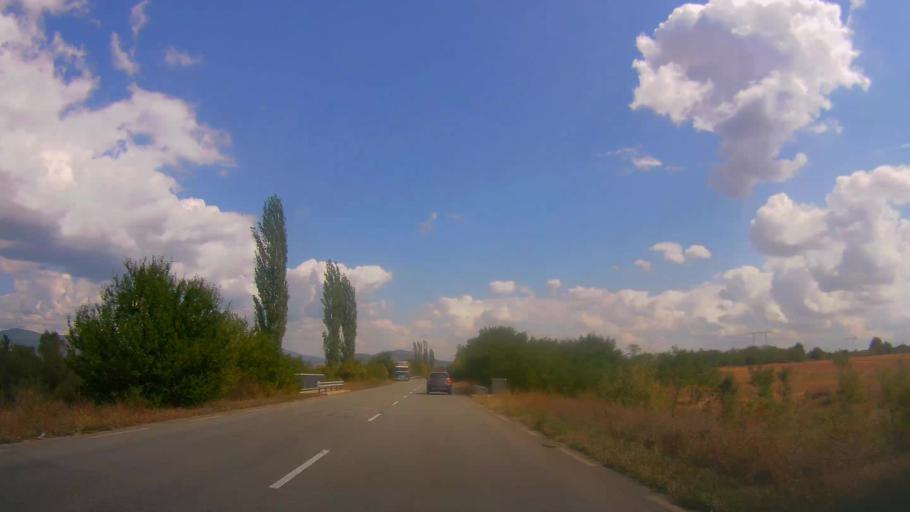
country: BG
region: Sliven
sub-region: Obshtina Tvurditsa
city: Tvurditsa
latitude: 42.6536
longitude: 25.9595
